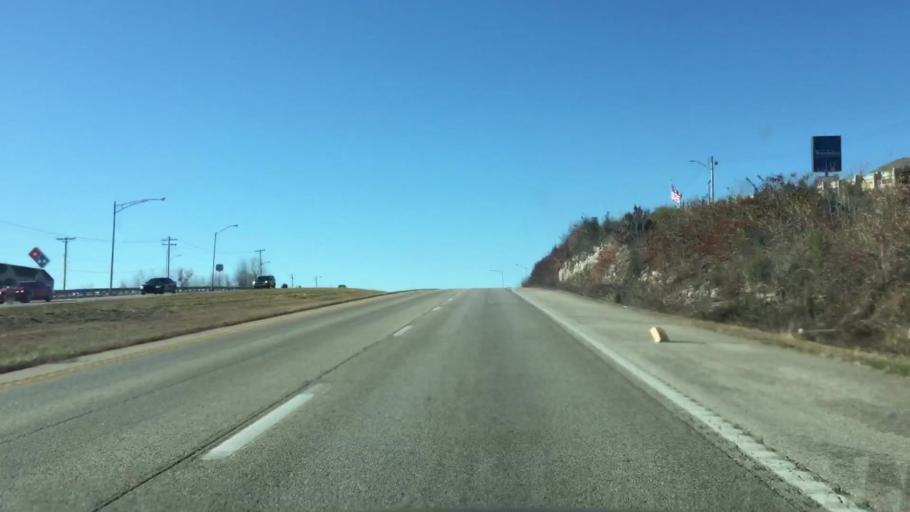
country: US
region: Missouri
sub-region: Cole County
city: Jefferson City
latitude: 38.5571
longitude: -92.1936
